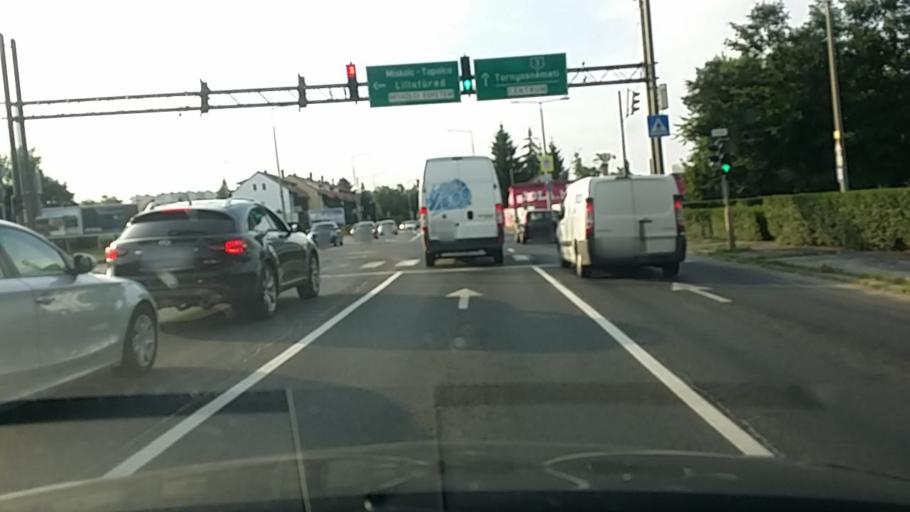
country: HU
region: Borsod-Abauj-Zemplen
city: Miskolc
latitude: 48.0664
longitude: 20.7925
